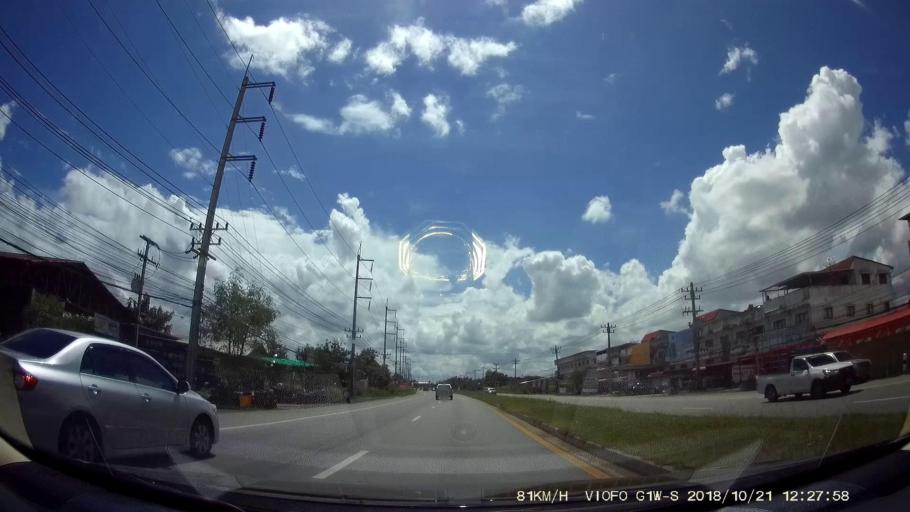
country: TH
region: Nakhon Ratchasima
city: Dan Khun Thot
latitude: 15.1953
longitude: 101.7621
